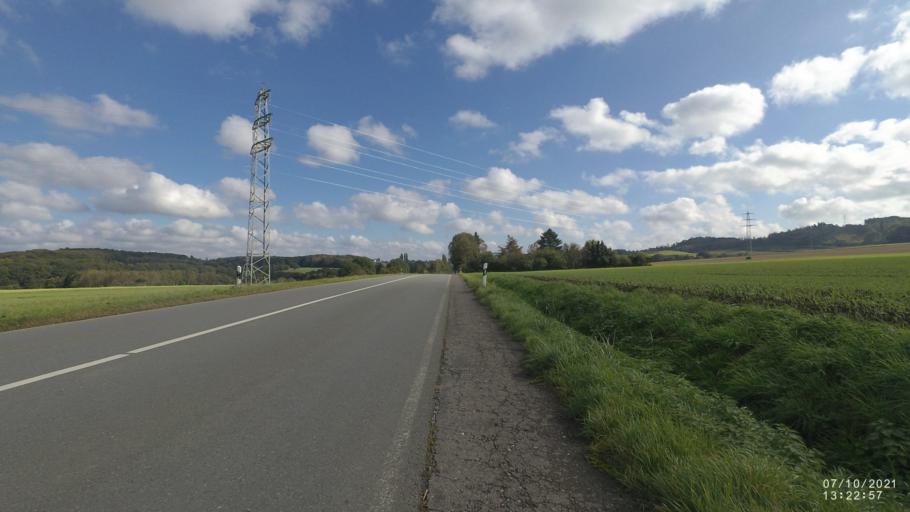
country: DE
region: North Rhine-Westphalia
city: Iserlohn
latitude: 51.4029
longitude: 7.7277
